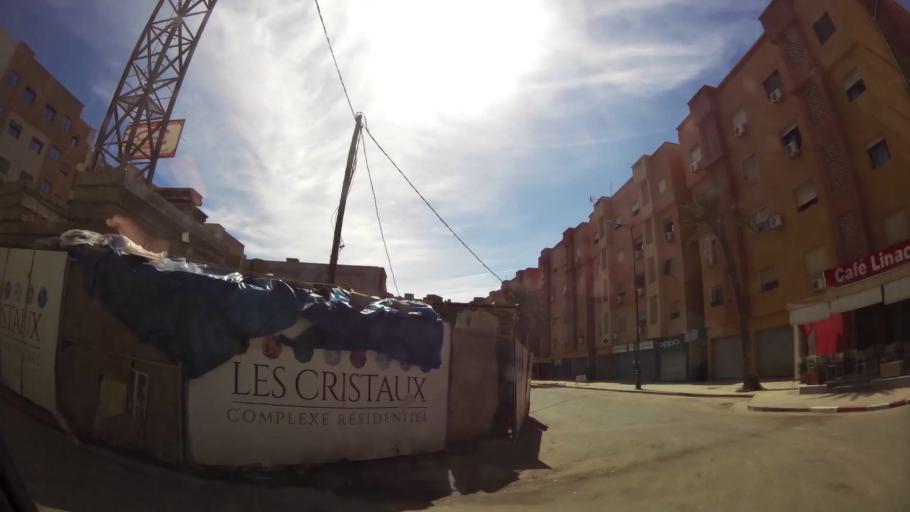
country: MA
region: Marrakech-Tensift-Al Haouz
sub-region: Marrakech
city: Marrakesh
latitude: 31.6594
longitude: -8.0206
